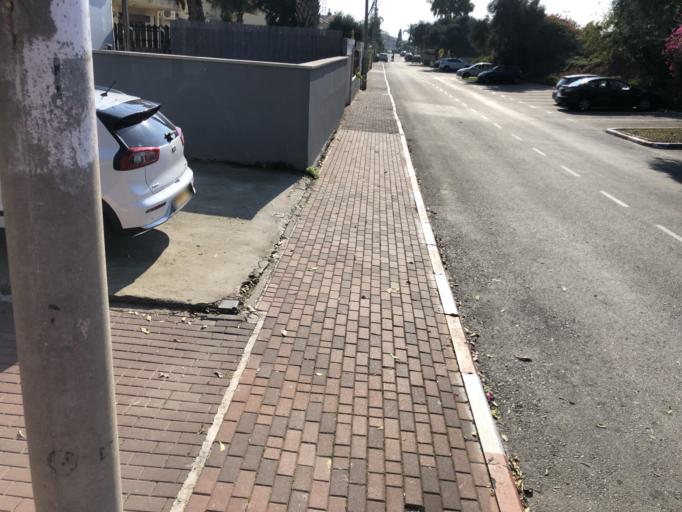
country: IL
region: Northern District
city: `Akko
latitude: 32.9202
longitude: 35.0907
